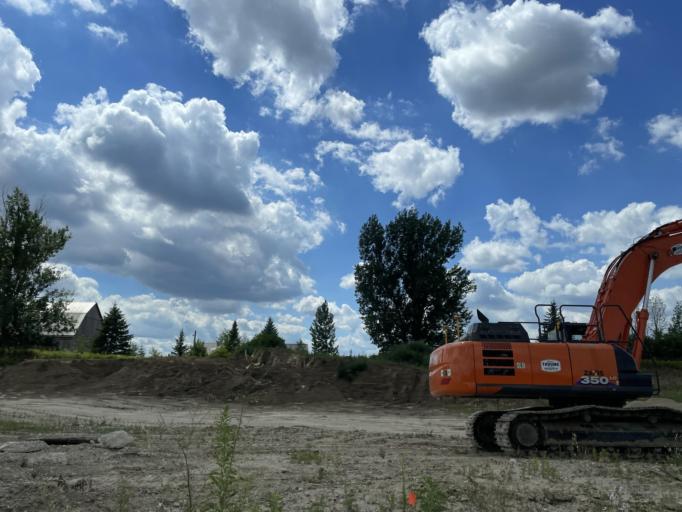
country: CA
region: Ontario
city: Waterloo
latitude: 43.5360
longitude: -80.3998
